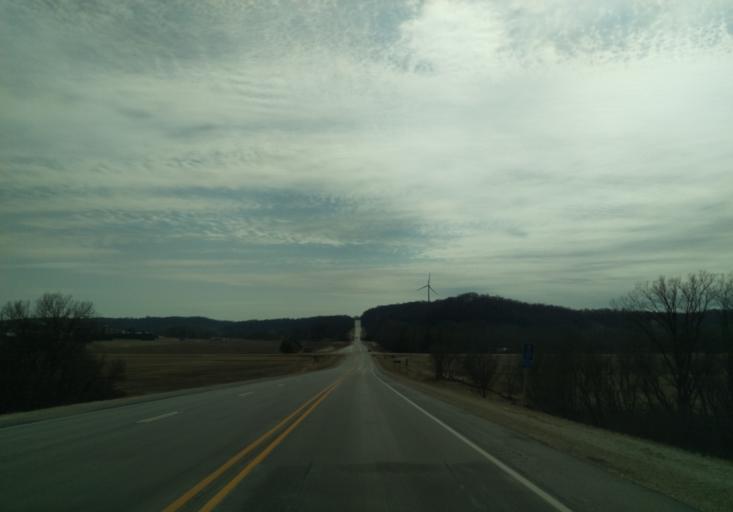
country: US
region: Iowa
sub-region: Winneshiek County
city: Decorah
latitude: 43.3244
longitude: -91.8135
